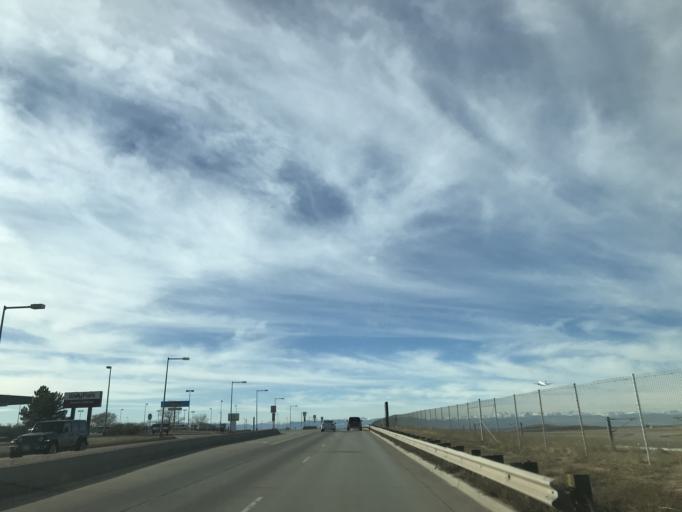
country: US
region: Colorado
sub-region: Adams County
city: Aurora
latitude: 39.8382
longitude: -104.7063
